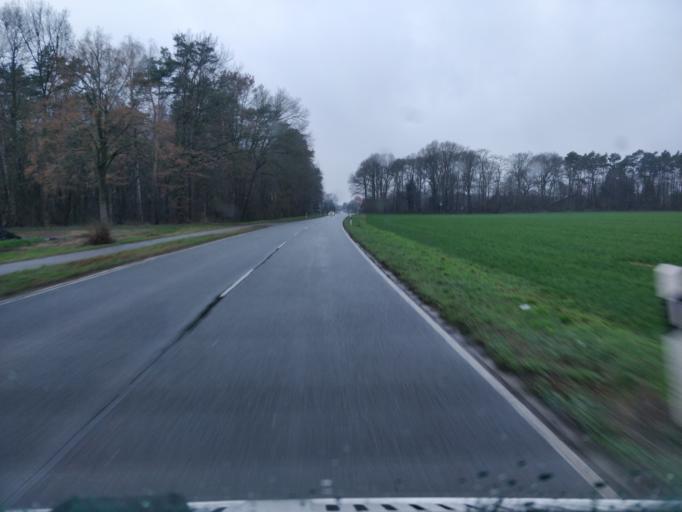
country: DE
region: North Rhine-Westphalia
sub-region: Regierungsbezirk Dusseldorf
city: Mehrhoog
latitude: 51.7427
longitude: 6.5373
